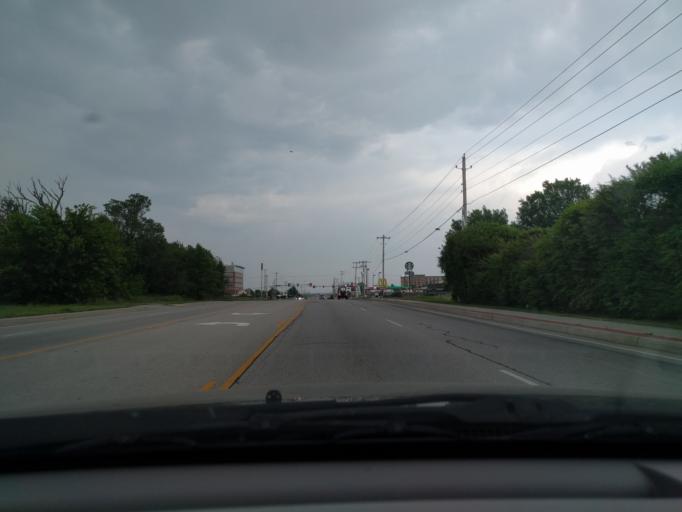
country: US
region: Oklahoma
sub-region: Tulsa County
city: Broken Arrow
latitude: 36.0464
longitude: -95.8712
